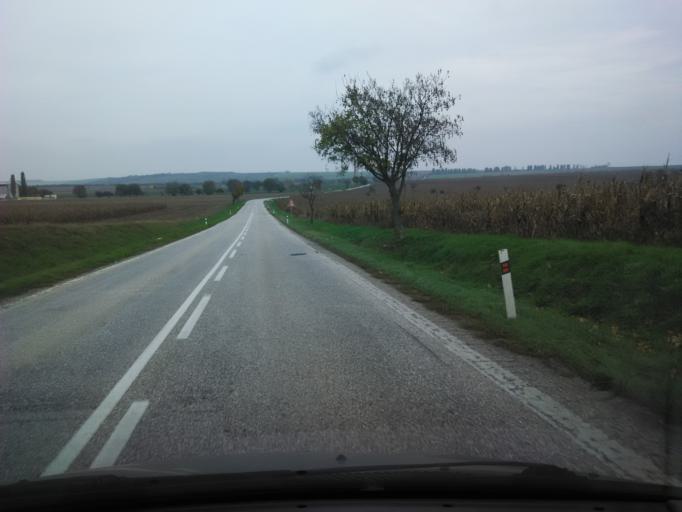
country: SK
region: Nitriansky
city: Svodin
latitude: 47.9974
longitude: 18.3454
